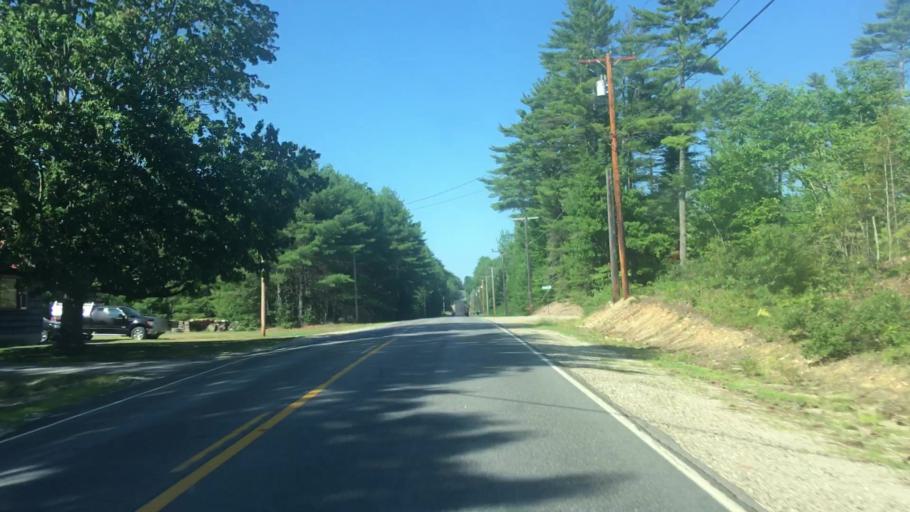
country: US
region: Maine
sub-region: York County
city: Buxton
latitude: 43.7006
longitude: -70.5854
